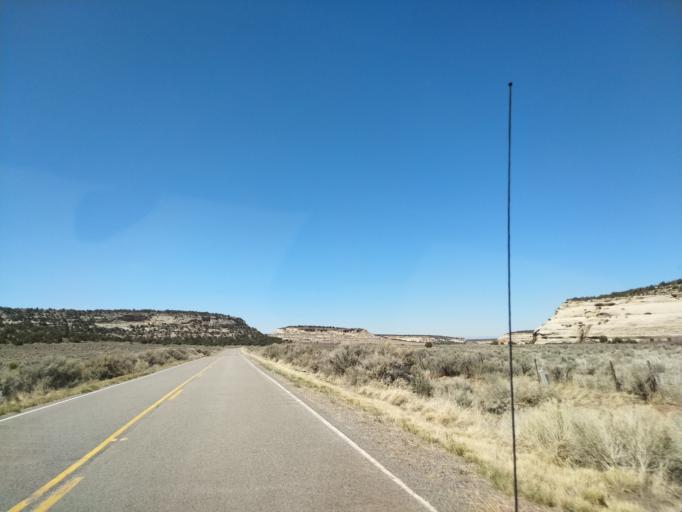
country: US
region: Colorado
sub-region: Mesa County
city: Redlands
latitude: 38.9829
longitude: -108.7981
